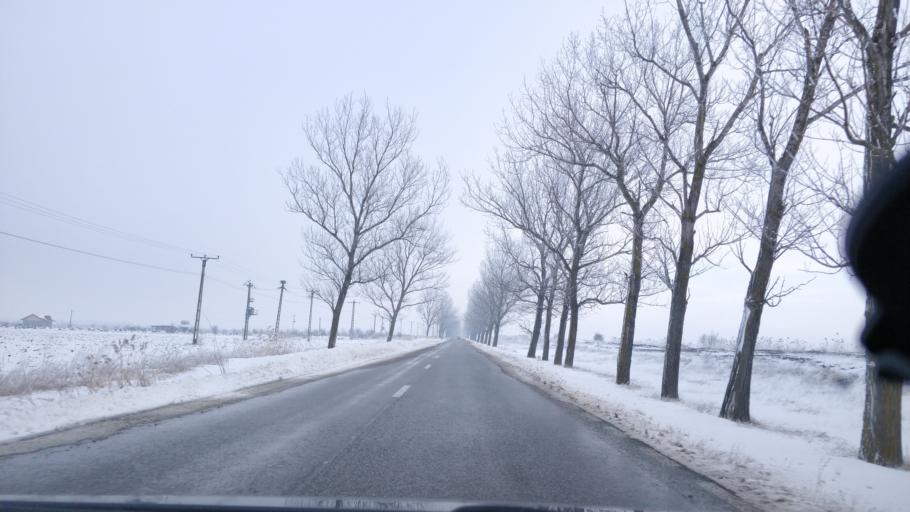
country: RO
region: Vrancea
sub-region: Comuna Vanatori
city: Jorasti
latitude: 45.6975
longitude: 27.2462
